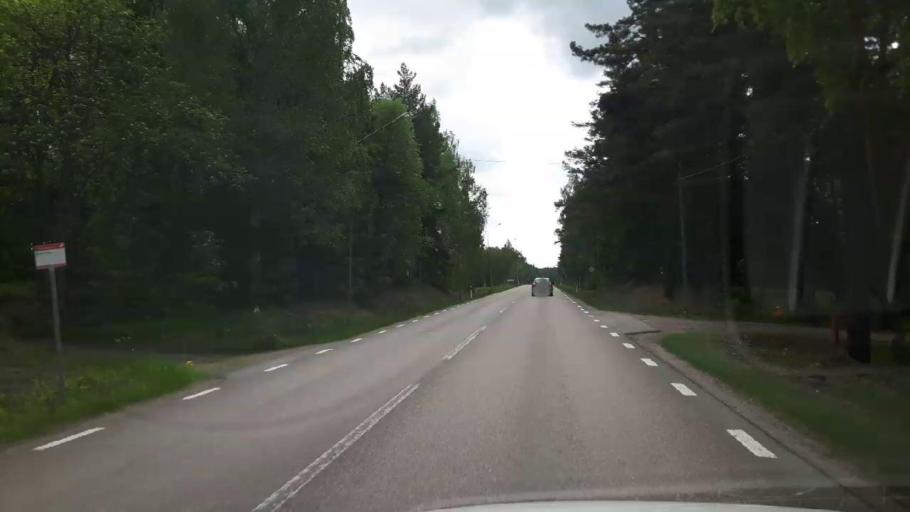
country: SE
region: Dalarna
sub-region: Faluns Kommun
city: Falun
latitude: 60.5168
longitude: 15.7350
